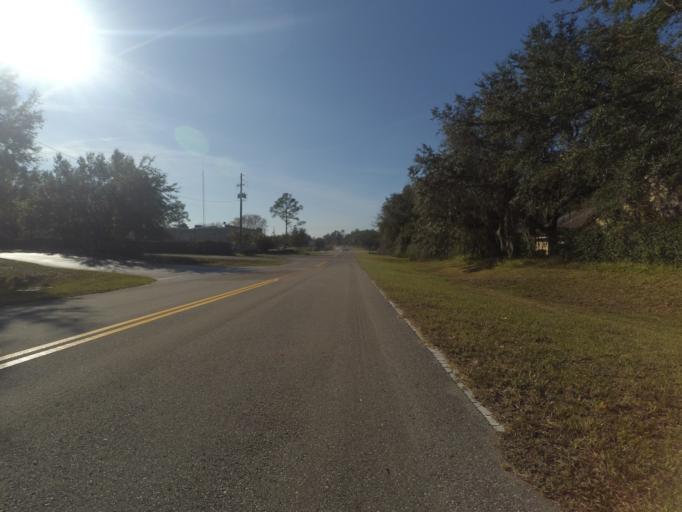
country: US
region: Florida
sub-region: Alachua County
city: Gainesville
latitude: 29.6093
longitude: -82.3699
